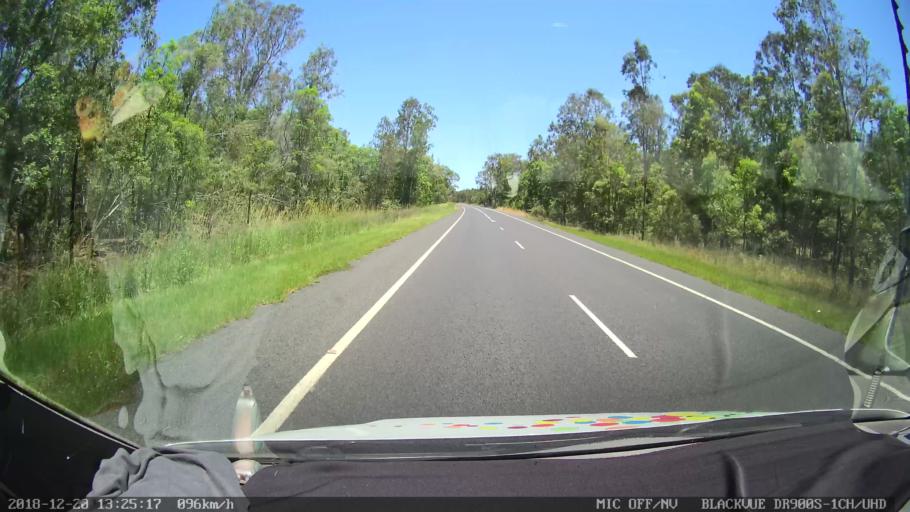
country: AU
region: New South Wales
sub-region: Richmond Valley
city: Casino
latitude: -29.1291
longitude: 152.9969
